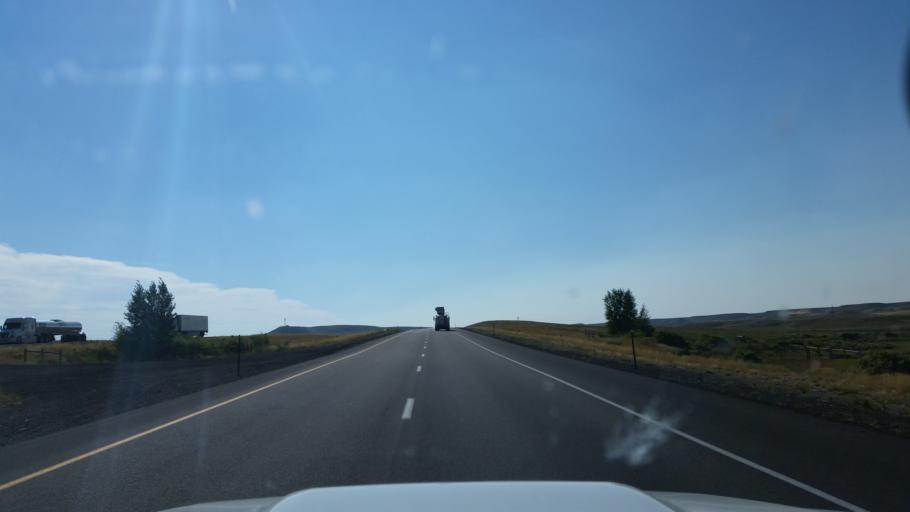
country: US
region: Wyoming
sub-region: Uinta County
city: Lyman
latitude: 41.3549
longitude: -110.3625
